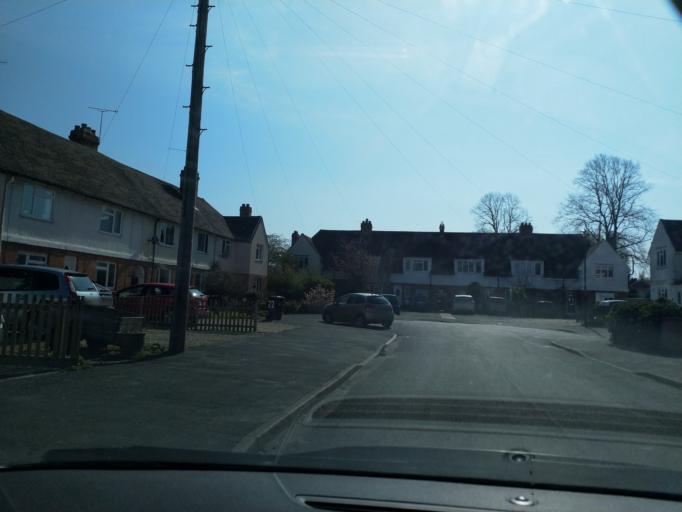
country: GB
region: England
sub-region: Warwickshire
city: Stratford-upon-Avon
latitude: 52.1857
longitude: -1.7179
